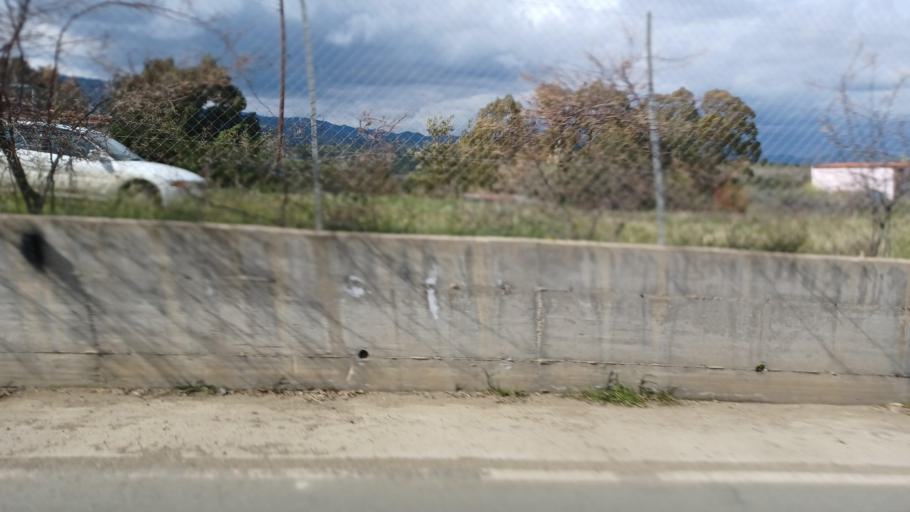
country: CY
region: Lefkosia
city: Lefka
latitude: 35.0807
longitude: 32.8935
